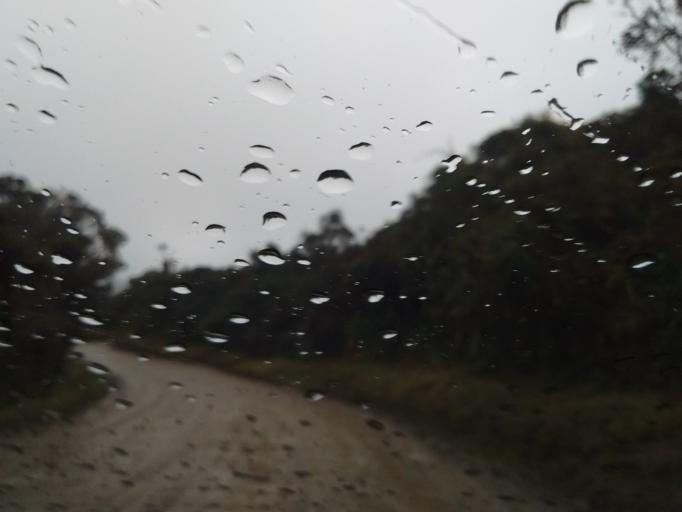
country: CO
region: Cauca
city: Paispamba
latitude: 2.1661
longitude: -76.4067
